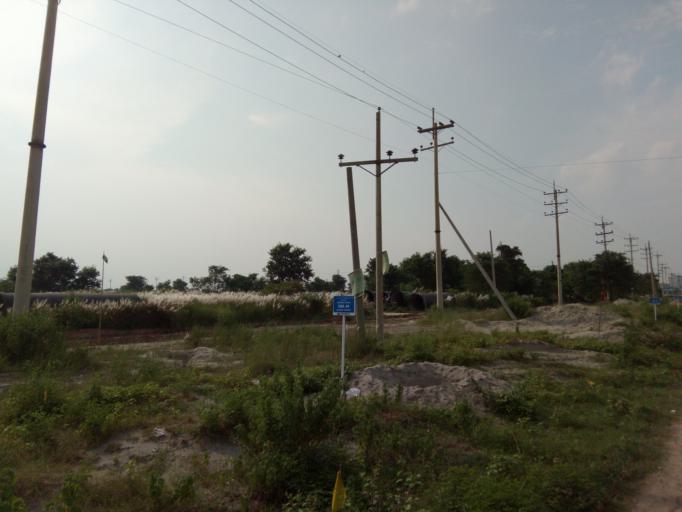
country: BD
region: Dhaka
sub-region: Dhaka
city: Dhaka
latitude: 23.6788
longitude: 90.4038
